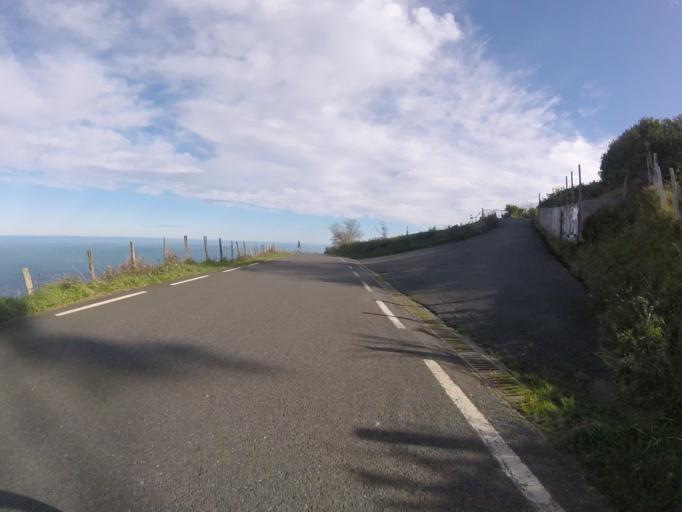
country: ES
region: Basque Country
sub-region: Provincia de Guipuzcoa
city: Usurbil
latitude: 43.2995
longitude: -2.0683
